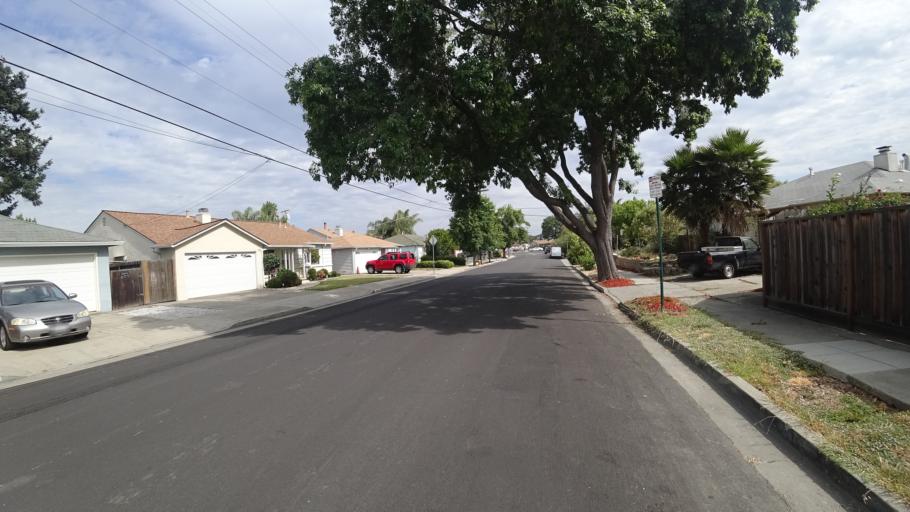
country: US
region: California
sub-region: Alameda County
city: Hayward
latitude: 37.6487
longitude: -122.0743
